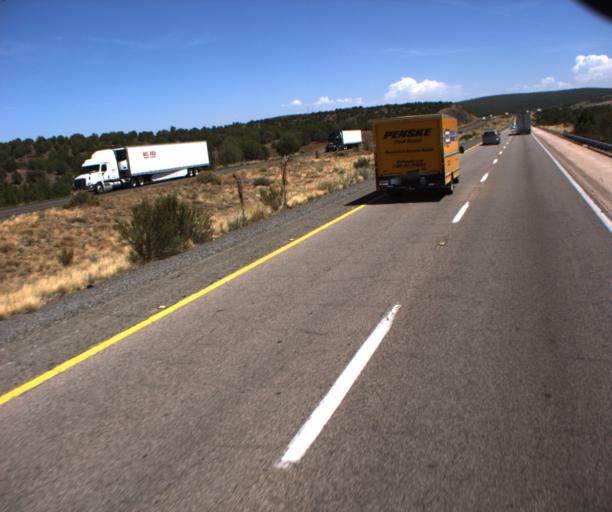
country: US
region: Arizona
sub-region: Mohave County
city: Peach Springs
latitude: 35.1953
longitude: -113.3076
